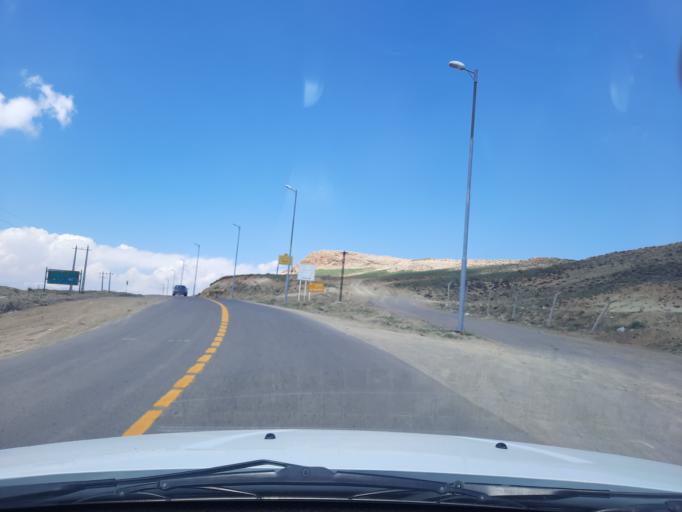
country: IR
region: Qazvin
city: Qazvin
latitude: 36.3845
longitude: 50.2066
